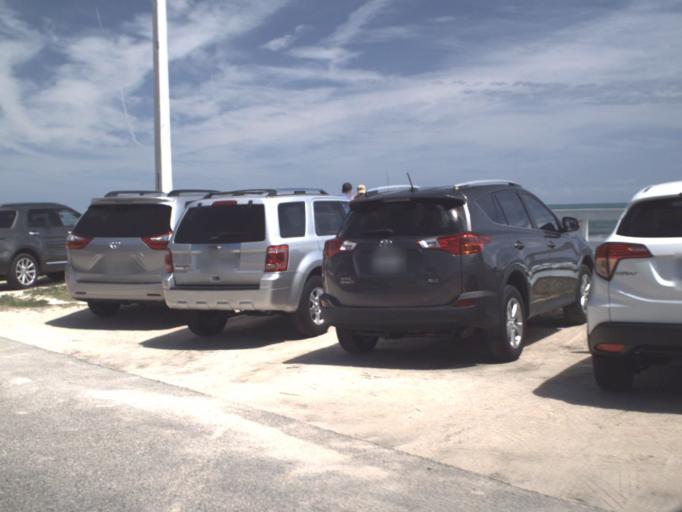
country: US
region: Florida
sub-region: Flagler County
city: Flagler Beach
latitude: 29.4773
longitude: -81.1256
